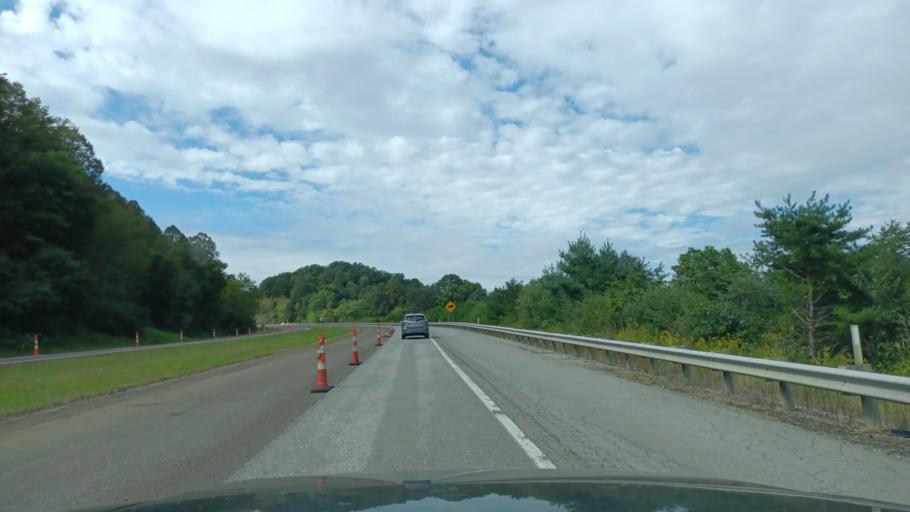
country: US
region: West Virginia
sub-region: Ritchie County
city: Harrisville
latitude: 39.2601
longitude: -81.1189
